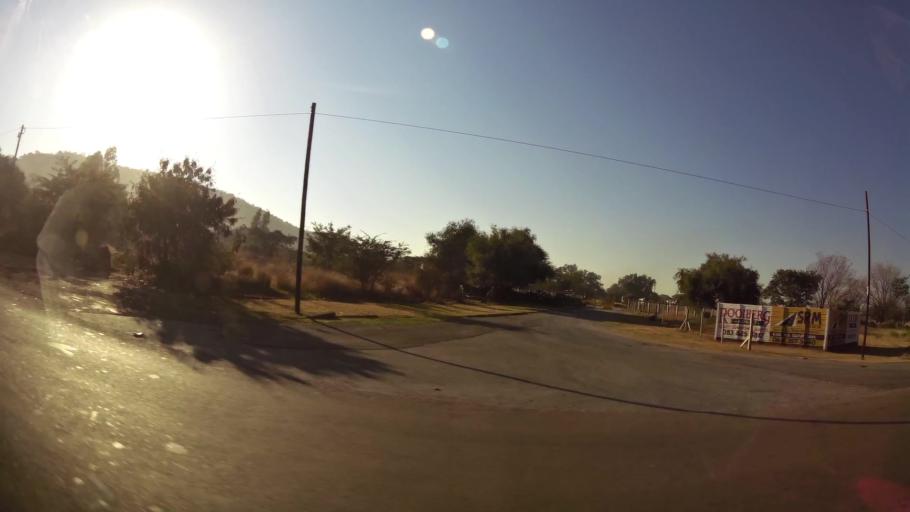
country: ZA
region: Gauteng
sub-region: City of Tshwane Metropolitan Municipality
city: Pretoria
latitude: -25.6328
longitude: 28.2047
